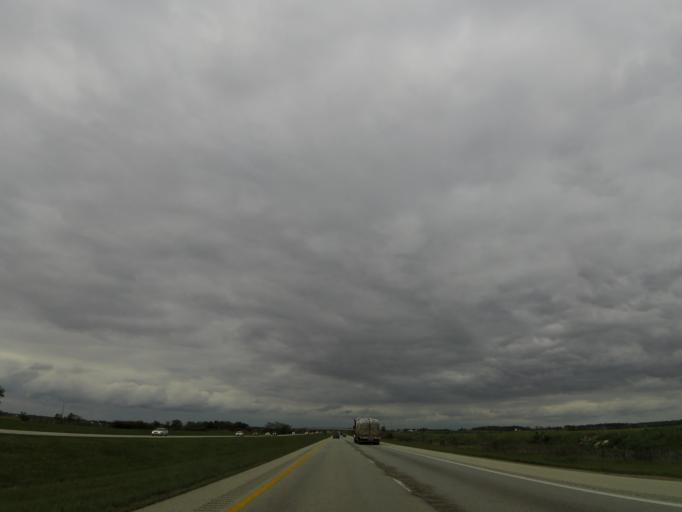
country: US
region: Ohio
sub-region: Greene County
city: Shawnee Hills
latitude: 39.5444
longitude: -83.7572
